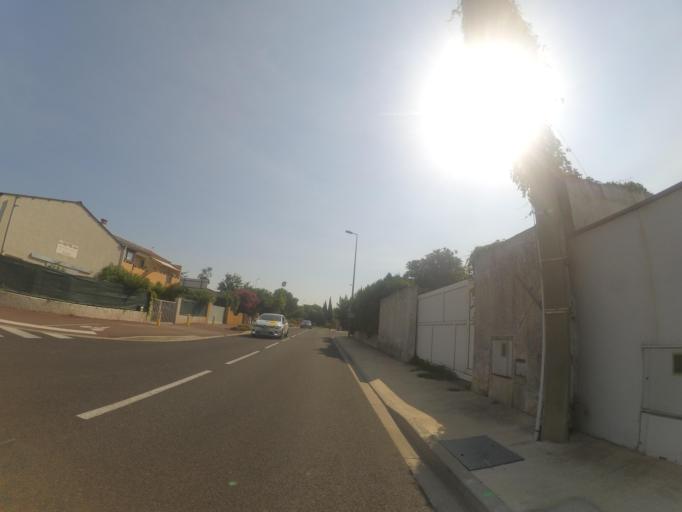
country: FR
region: Languedoc-Roussillon
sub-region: Departement des Pyrenees-Orientales
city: Toulouges
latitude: 42.6627
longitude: 2.8319
